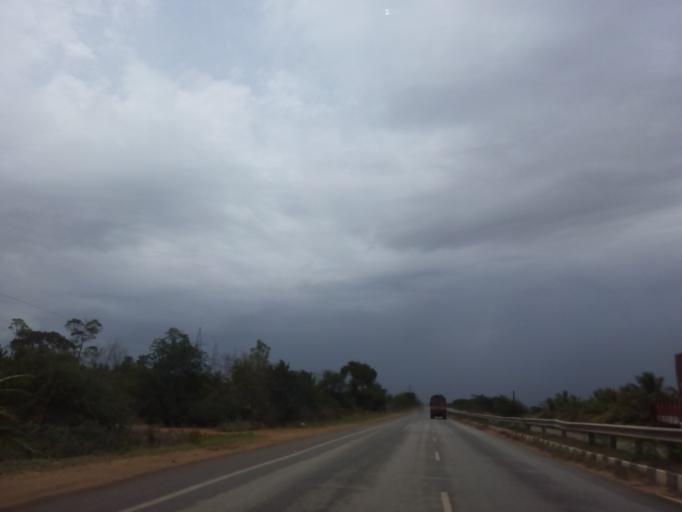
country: IN
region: Karnataka
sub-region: Davanagere
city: Harihar
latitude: 14.4802
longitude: 75.8116
